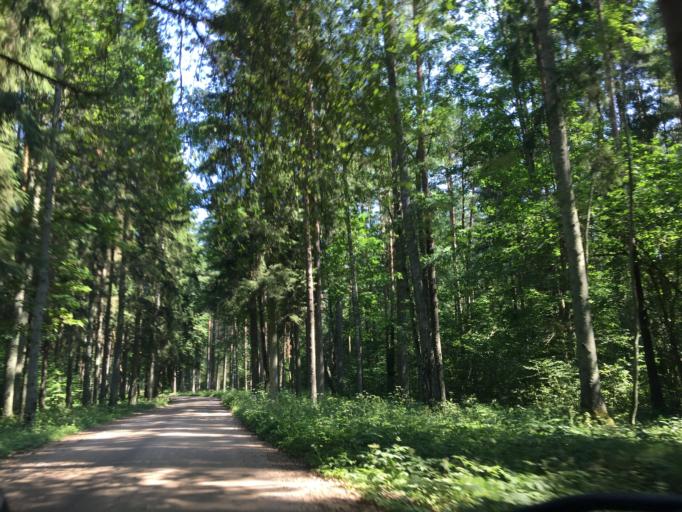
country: LV
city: Tervete
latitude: 56.4837
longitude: 23.3985
